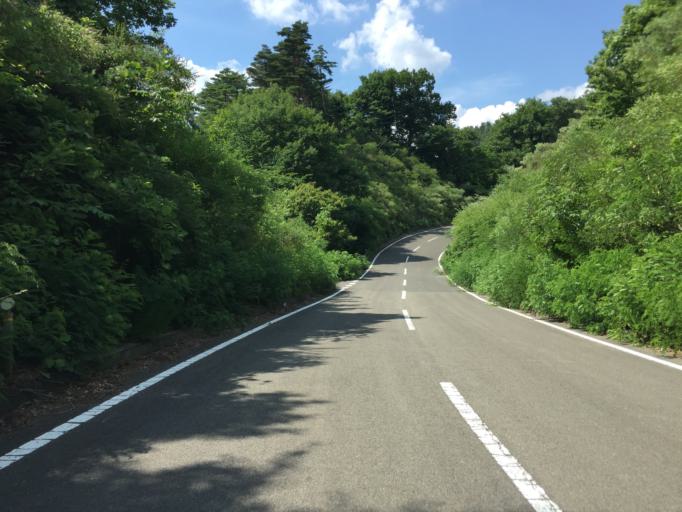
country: JP
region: Fukushima
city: Yanagawamachi-saiwaicho
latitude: 37.7666
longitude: 140.6738
